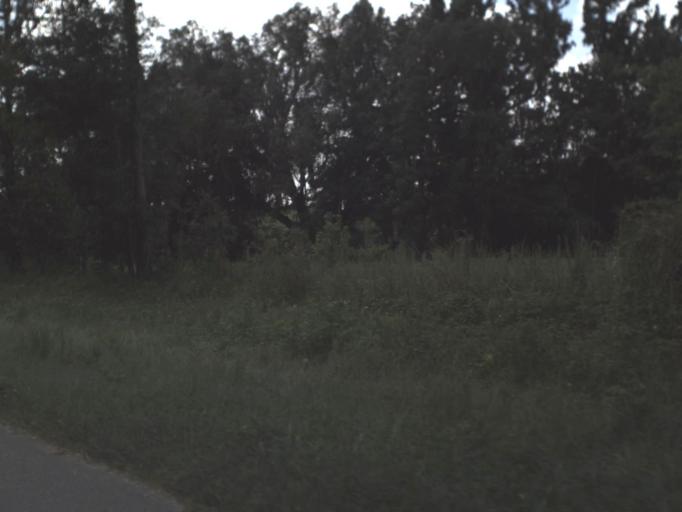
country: US
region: Florida
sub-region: Gilchrist County
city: Trenton
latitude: 29.6397
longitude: -82.8312
